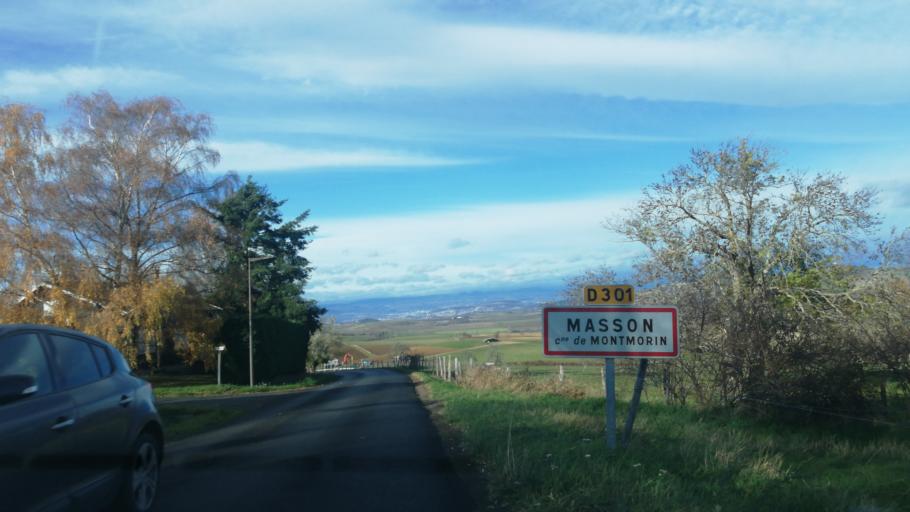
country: FR
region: Auvergne
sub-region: Departement du Puy-de-Dome
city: Billom
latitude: 45.7004
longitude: 3.3551
